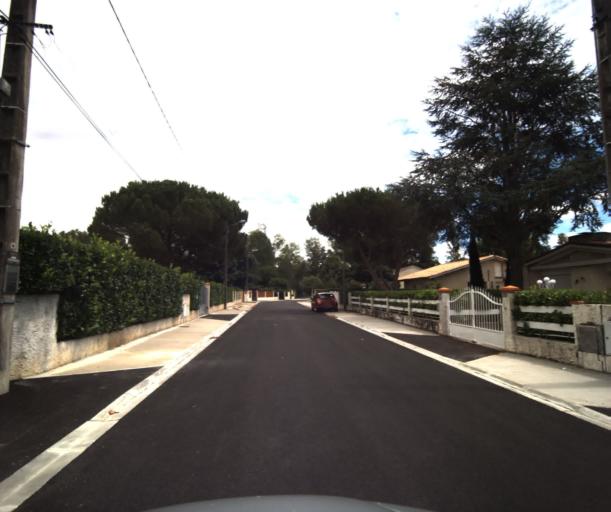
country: FR
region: Midi-Pyrenees
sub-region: Departement de la Haute-Garonne
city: Lacroix-Falgarde
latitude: 43.4800
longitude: 1.4072
